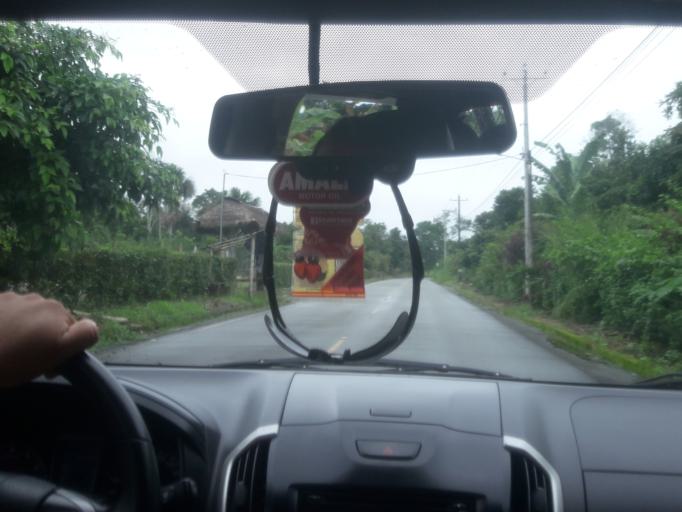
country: EC
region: Napo
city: Tena
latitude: -1.0436
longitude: -77.6984
